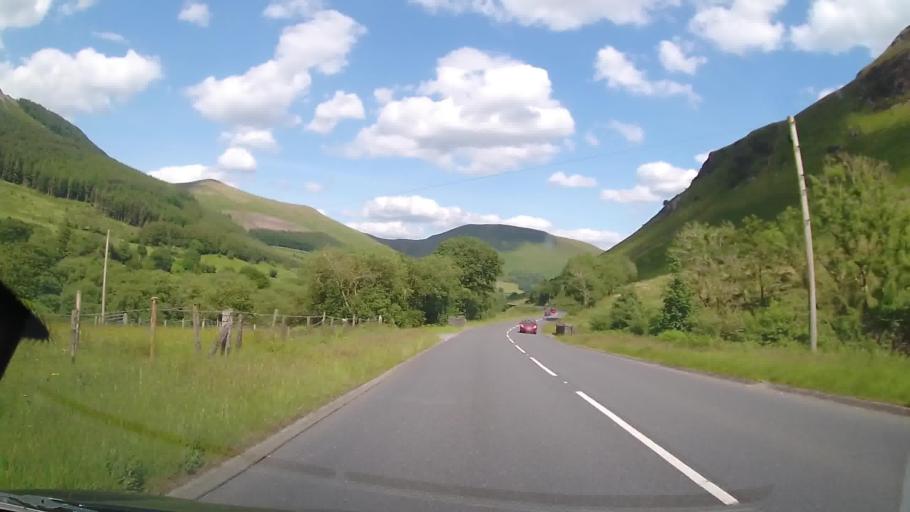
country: GB
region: Wales
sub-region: Gwynedd
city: Corris
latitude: 52.7324
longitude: -3.7433
